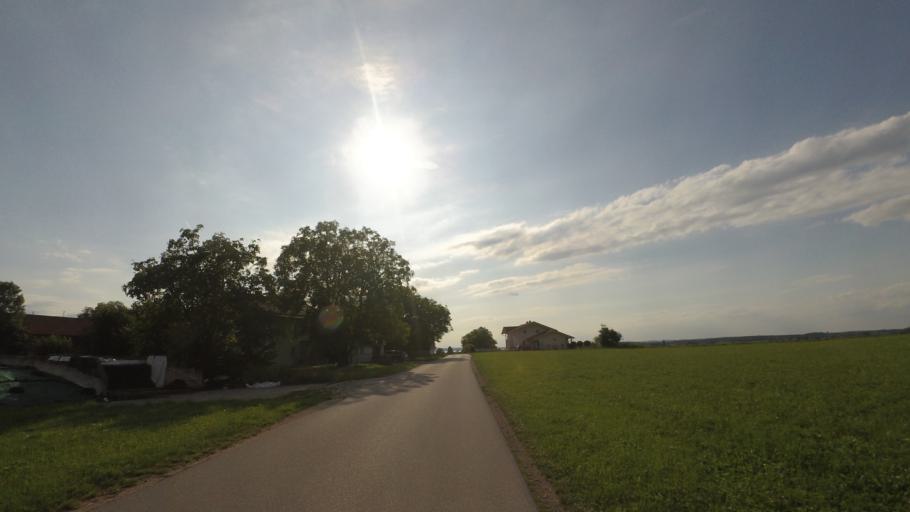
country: DE
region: Bavaria
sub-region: Upper Bavaria
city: Chieming
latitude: 47.8908
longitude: 12.5558
